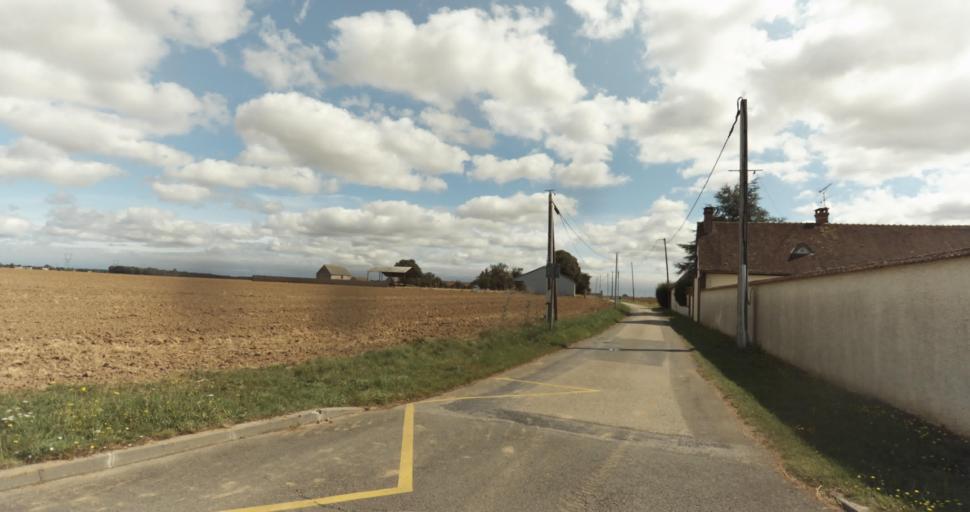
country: FR
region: Haute-Normandie
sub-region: Departement de l'Eure
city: Damville
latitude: 48.8546
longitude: 1.1612
